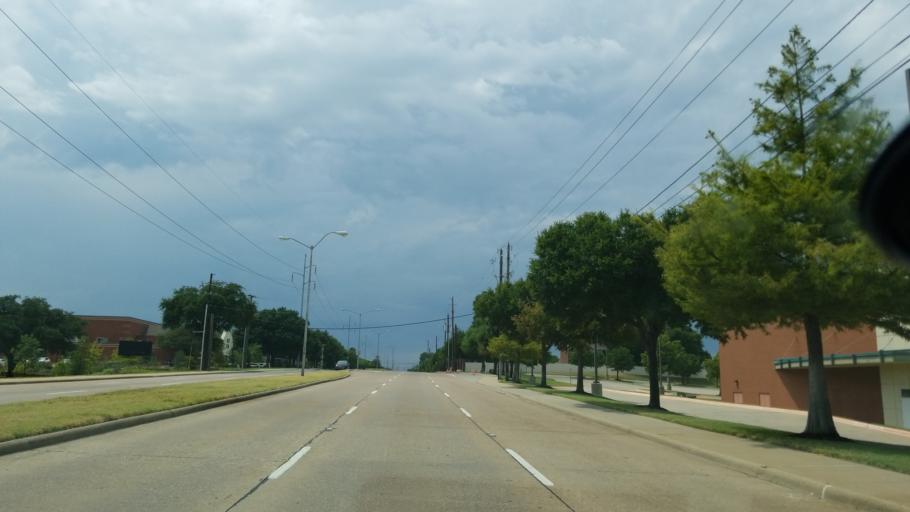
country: US
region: Texas
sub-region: Dallas County
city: Duncanville
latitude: 32.6623
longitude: -96.8473
